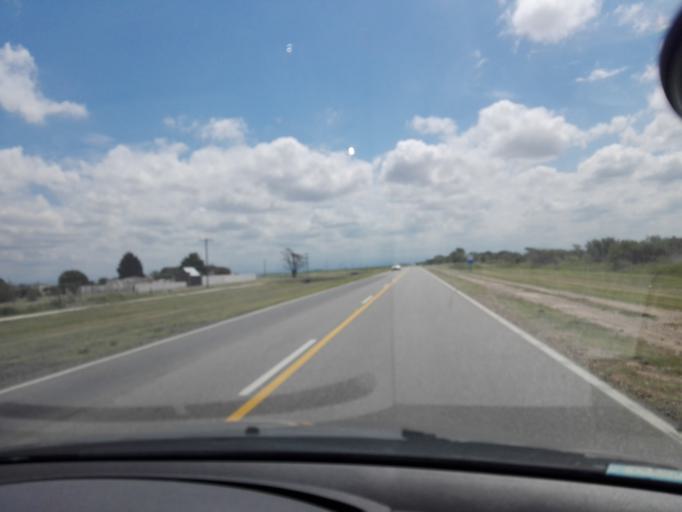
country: AR
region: Cordoba
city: Toledo
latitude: -31.6484
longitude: -64.1051
